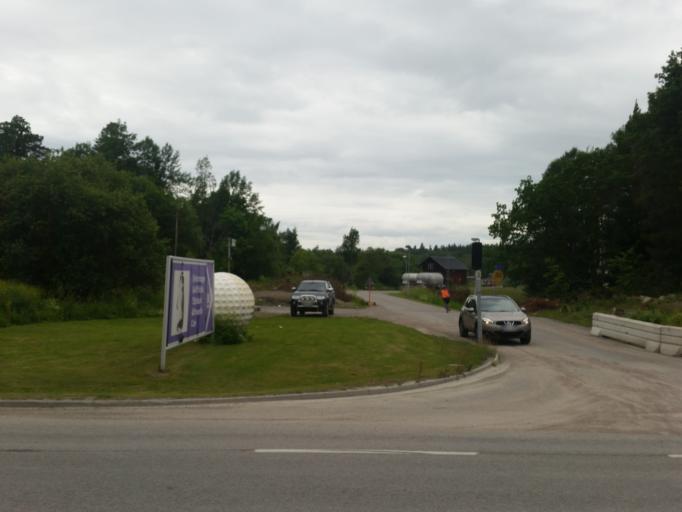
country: SE
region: Stockholm
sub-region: Stockholms Kommun
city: Kista
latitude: 59.4162
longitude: 17.9054
